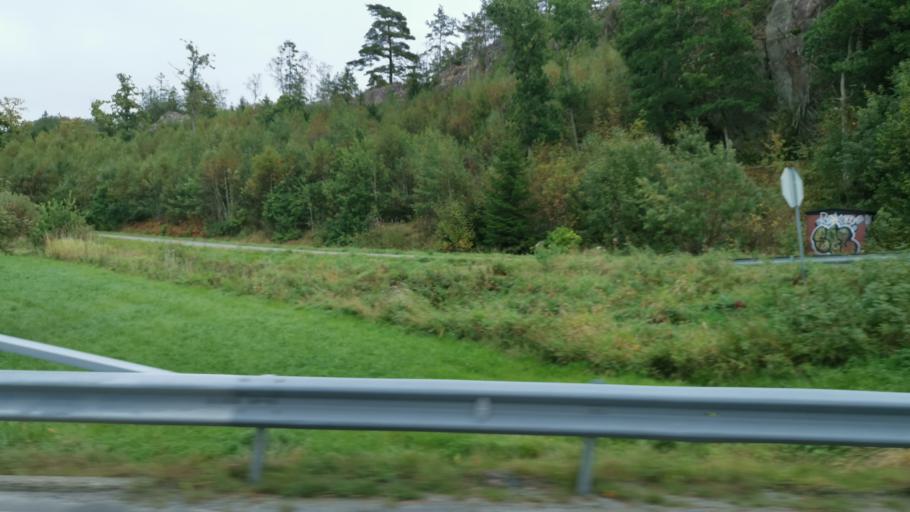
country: SE
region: Vaestra Goetaland
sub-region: Sotenas Kommun
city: Hunnebostrand
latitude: 58.5581
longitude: 11.4018
